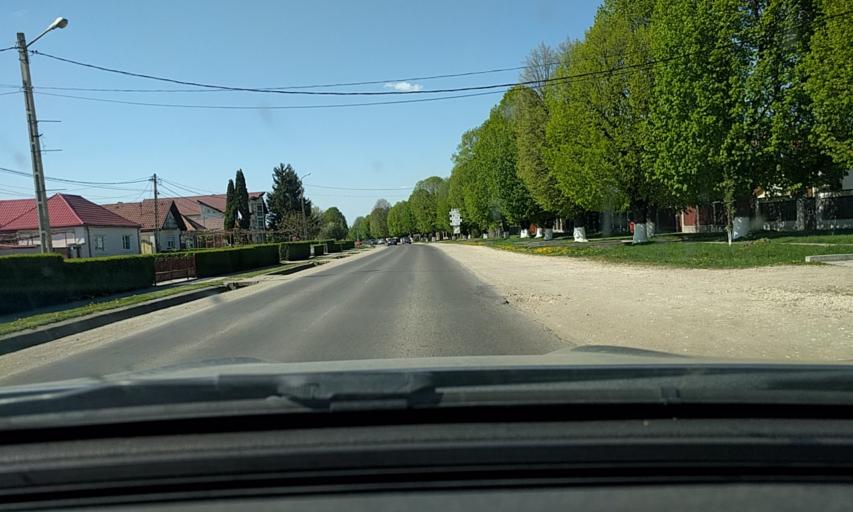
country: RO
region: Brasov
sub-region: Comuna Harman
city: Harman
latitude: 45.7068
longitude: 25.6873
